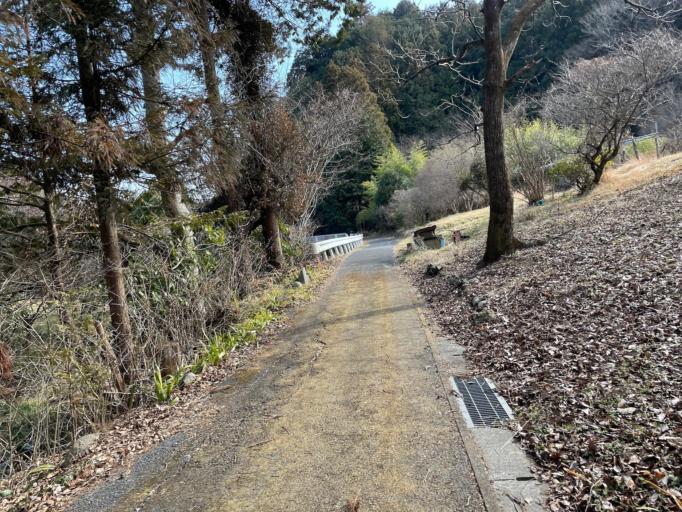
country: JP
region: Saitama
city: Hanno
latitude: 35.8449
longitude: 139.2620
